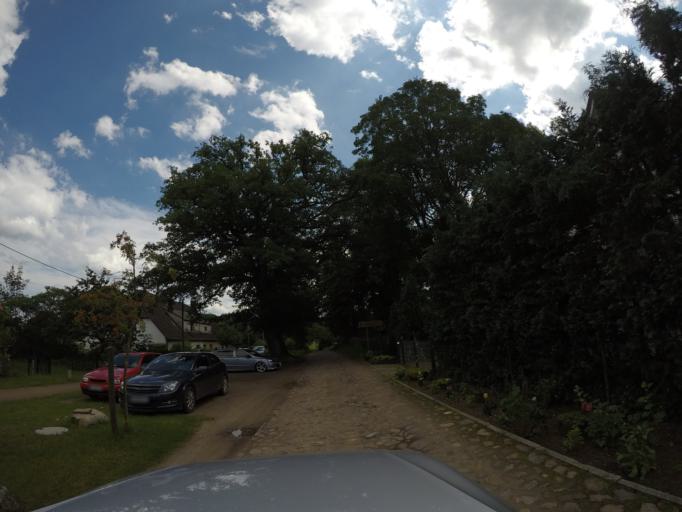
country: DE
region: Mecklenburg-Vorpommern
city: Mollenhagen
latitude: 53.4540
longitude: 12.9568
